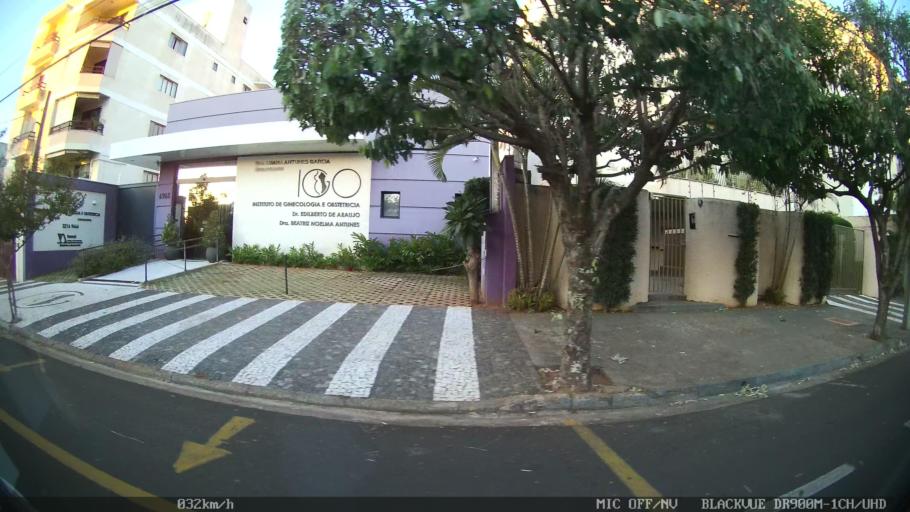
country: BR
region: Sao Paulo
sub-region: Sao Jose Do Rio Preto
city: Sao Jose do Rio Preto
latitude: -20.8457
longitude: -49.3934
